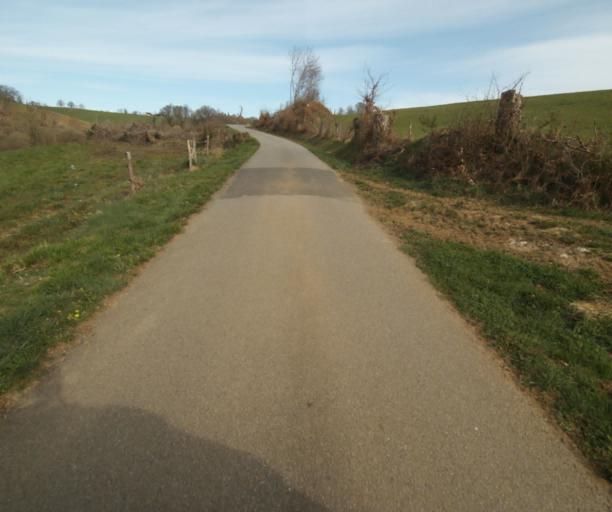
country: FR
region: Limousin
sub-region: Departement de la Correze
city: Chamboulive
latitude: 45.4167
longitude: 1.7908
